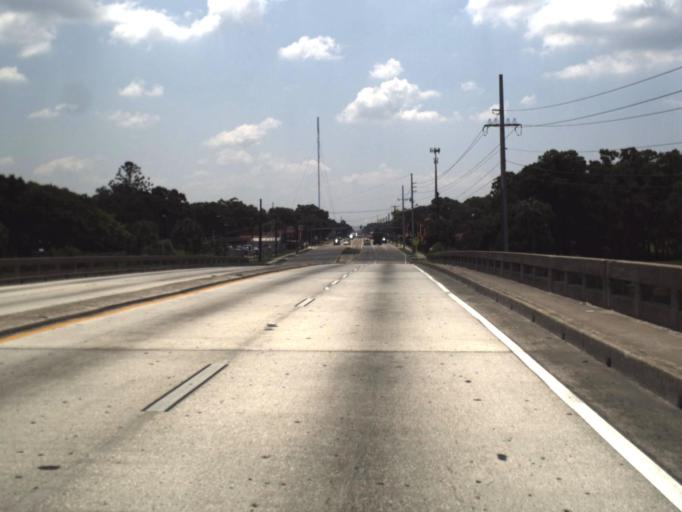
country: US
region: Florida
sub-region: Hillsborough County
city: Palm River-Clair Mel
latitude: 27.9460
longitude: -82.4019
